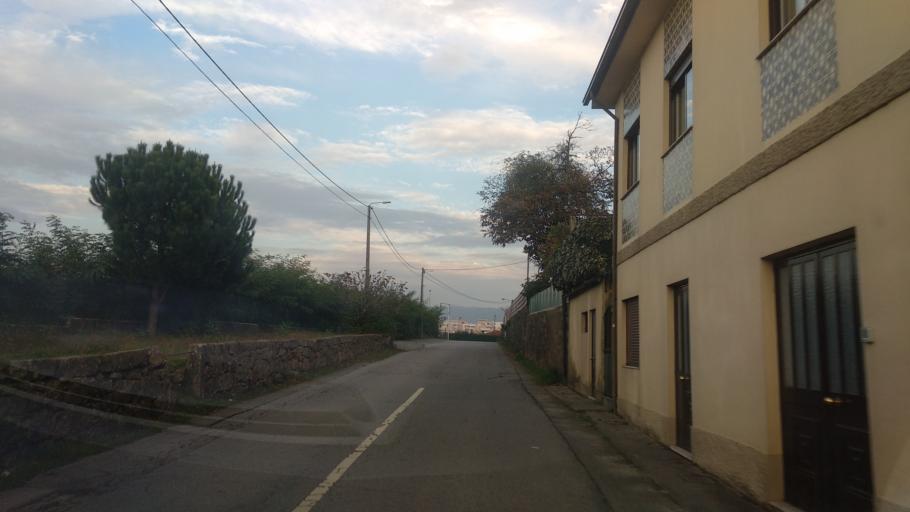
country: PT
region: Braga
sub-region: Braga
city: Braga
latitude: 41.5272
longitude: -8.4541
